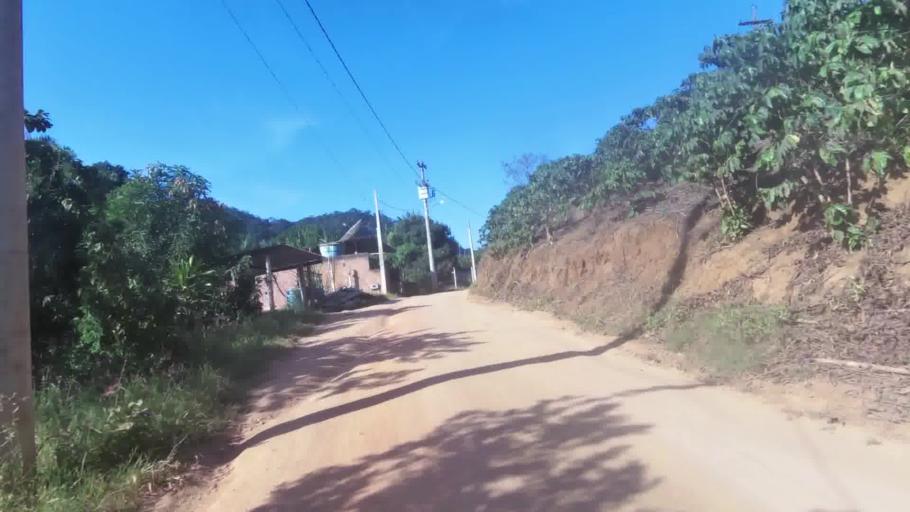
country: BR
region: Espirito Santo
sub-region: Iconha
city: Iconha
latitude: -20.7631
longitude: -40.8292
